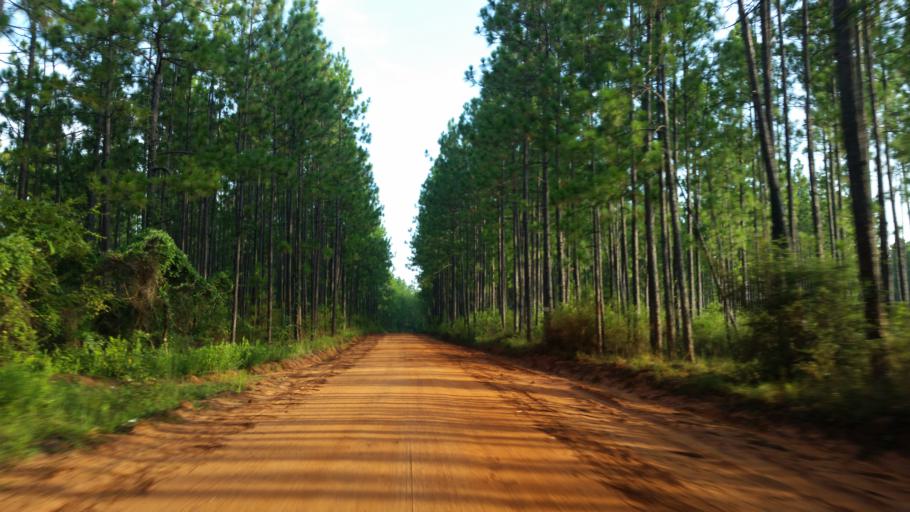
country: US
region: Alabama
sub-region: Escambia County
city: Atmore
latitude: 30.9481
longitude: -87.5718
